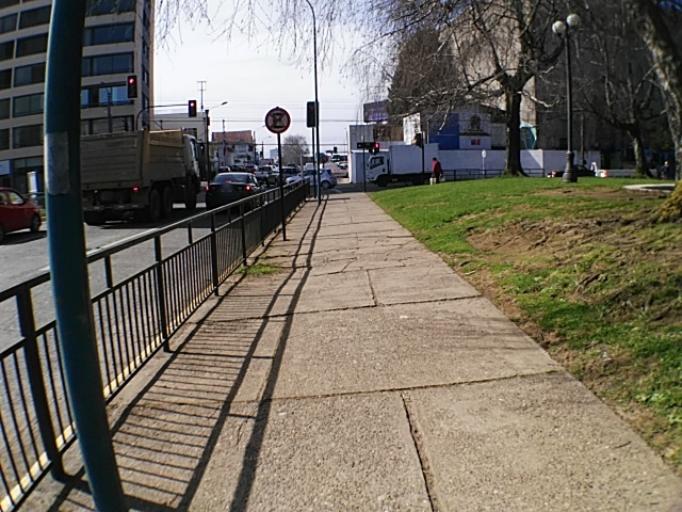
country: CL
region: Los Rios
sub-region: Provincia de Valdivia
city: Valdivia
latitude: -39.8121
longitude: -73.2462
